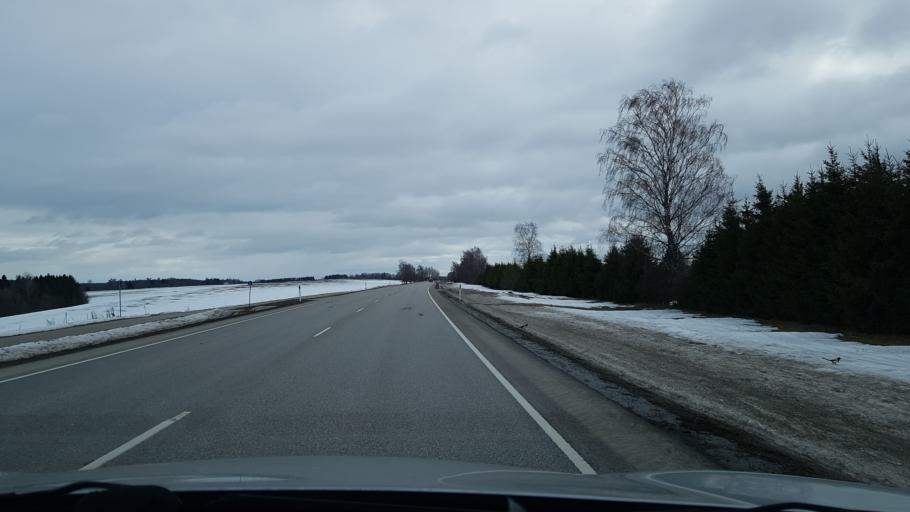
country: EE
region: Jogevamaa
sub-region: Tabivere vald
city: Tabivere
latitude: 58.6385
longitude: 26.5616
